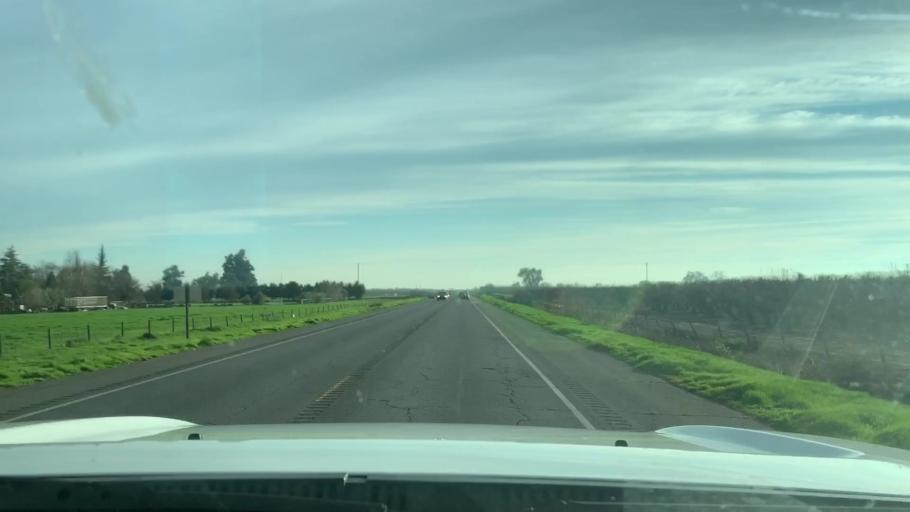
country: US
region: California
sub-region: Fresno County
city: Riverdale
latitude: 36.4155
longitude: -119.8044
